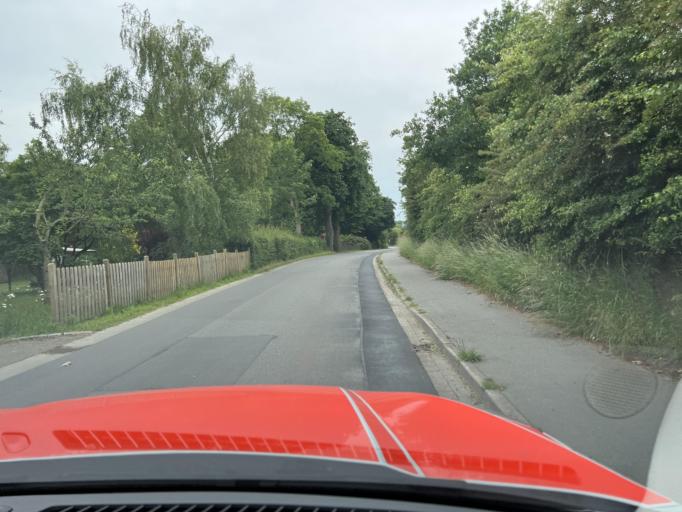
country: DE
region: Schleswig-Holstein
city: Hemmingstedt
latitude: 54.1624
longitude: 9.0924
